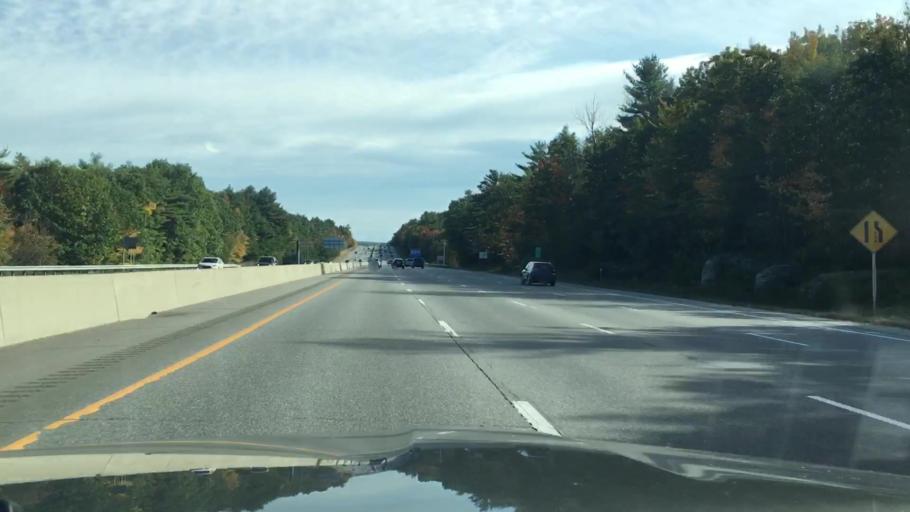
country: US
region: New Hampshire
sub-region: Merrimack County
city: Bow Bog
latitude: 43.1568
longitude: -71.5094
